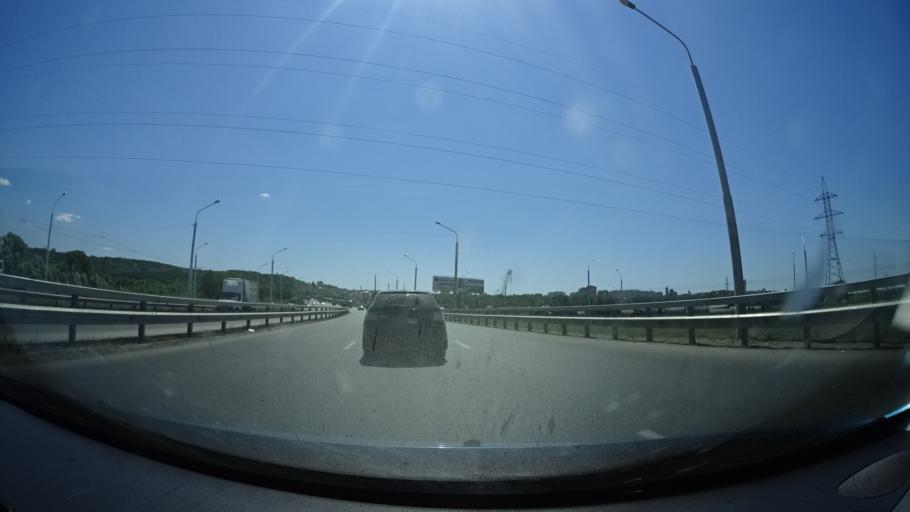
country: RU
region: Bashkortostan
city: Ufa
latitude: 54.7635
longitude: 55.9563
